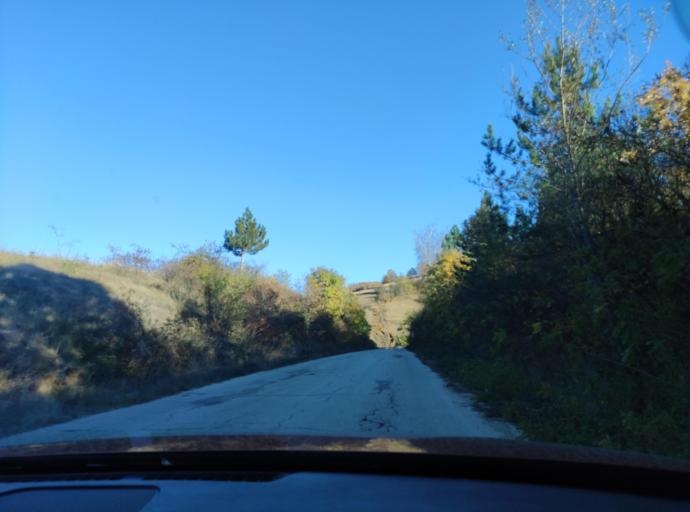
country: BG
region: Montana
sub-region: Obshtina Chiprovtsi
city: Chiprovtsi
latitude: 43.3795
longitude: 22.9112
